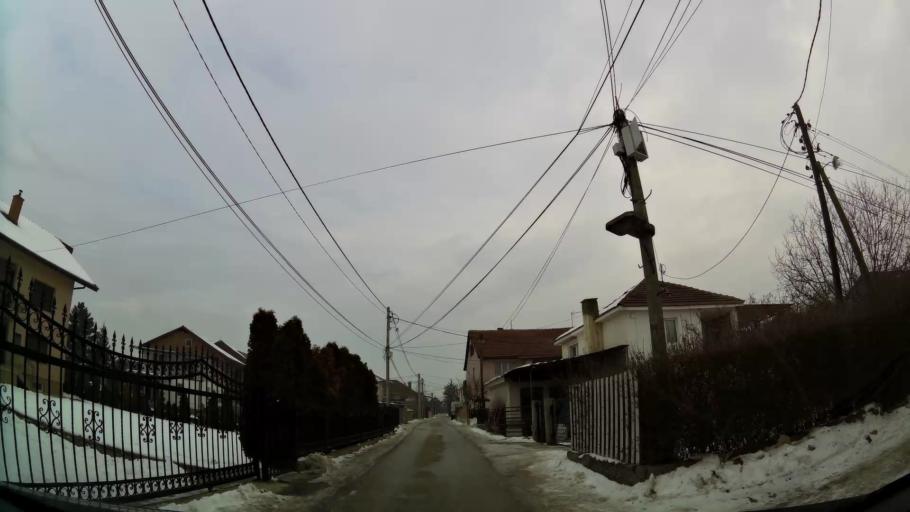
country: MK
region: Saraj
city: Saraj
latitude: 42.0471
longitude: 21.3585
